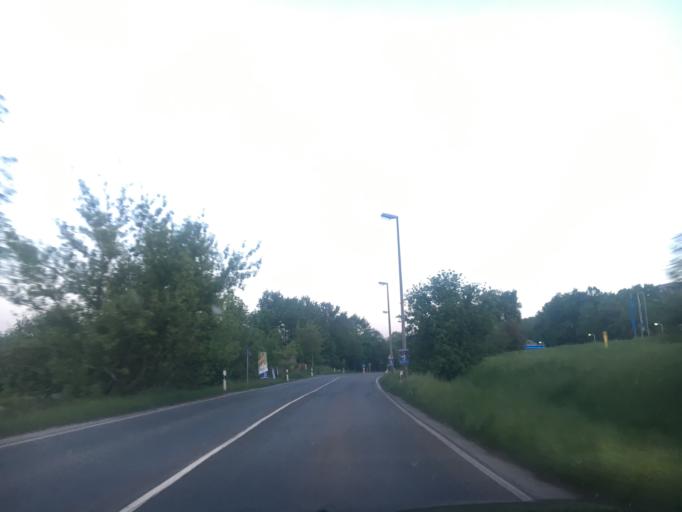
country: DE
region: Thuringia
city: Gera
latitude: 50.8450
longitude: 12.0779
